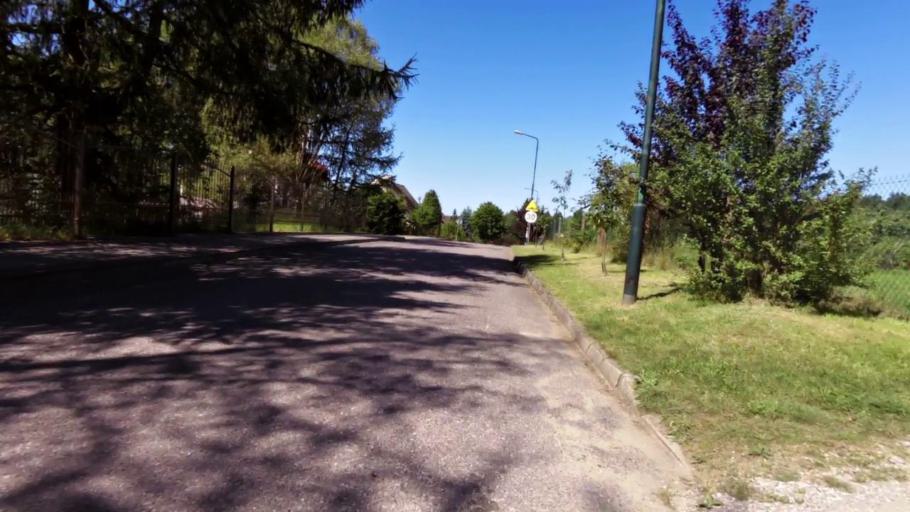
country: PL
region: West Pomeranian Voivodeship
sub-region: Powiat szczecinecki
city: Bialy Bor
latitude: 53.9009
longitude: 16.8319
